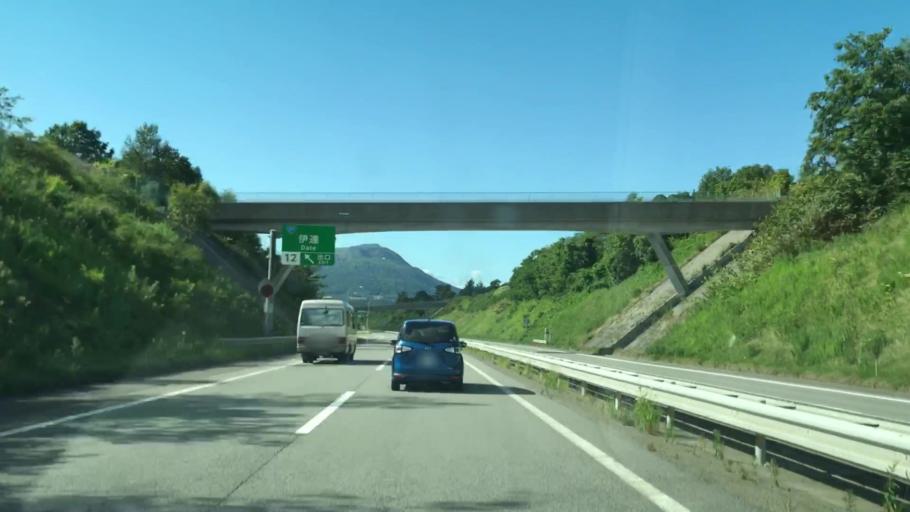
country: JP
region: Hokkaido
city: Date
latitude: 42.4783
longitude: 140.9004
